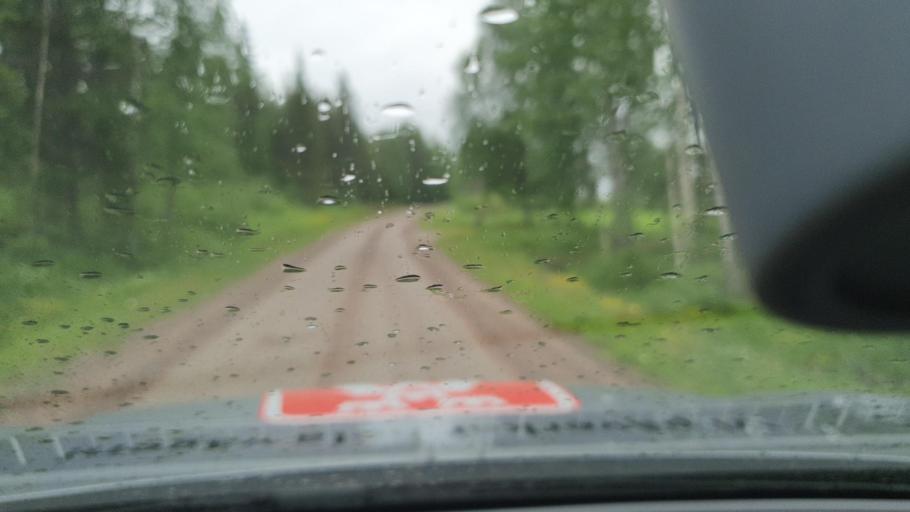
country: SE
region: Norrbotten
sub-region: Overkalix Kommun
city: OEverkalix
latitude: 66.5072
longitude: 22.7497
